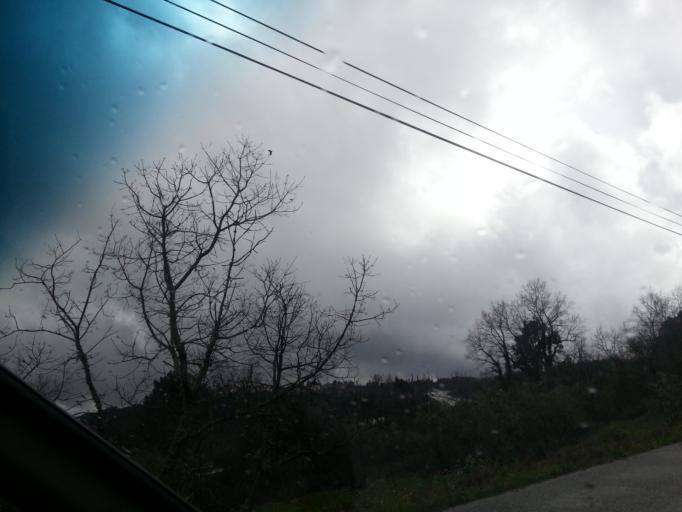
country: PT
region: Guarda
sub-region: Fornos de Algodres
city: Fornos de Algodres
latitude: 40.6225
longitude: -7.6021
